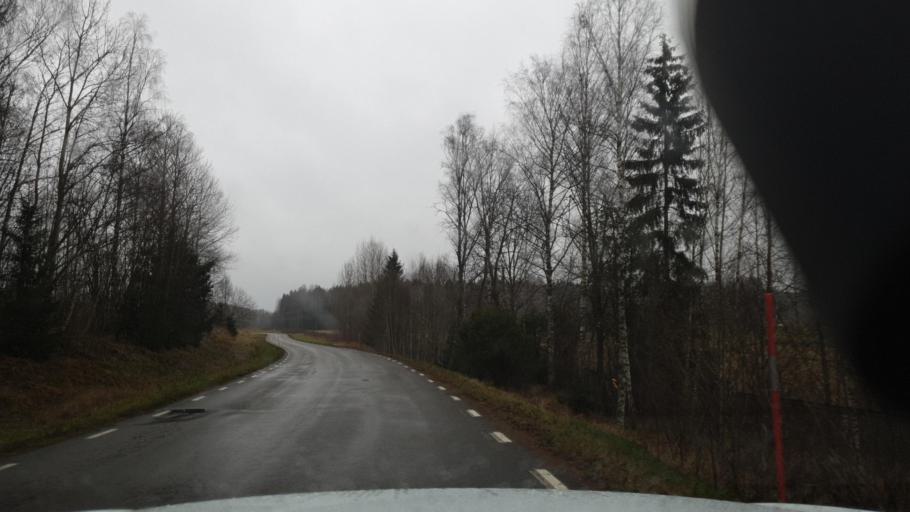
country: SE
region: Vaermland
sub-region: Eda Kommun
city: Amotfors
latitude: 59.7133
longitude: 12.4408
